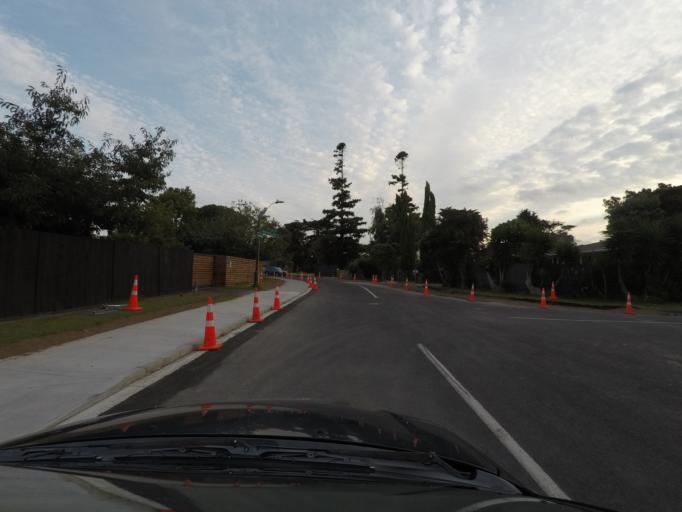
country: NZ
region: Auckland
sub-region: Auckland
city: Rosebank
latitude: -36.8358
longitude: 174.6533
